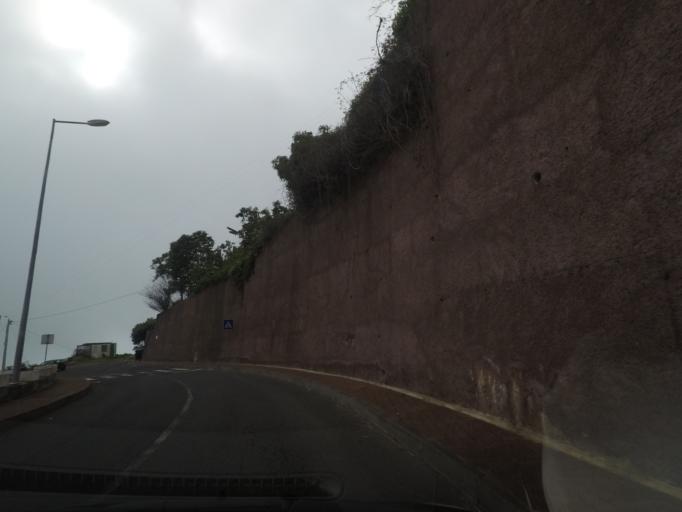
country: PT
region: Madeira
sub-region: Ribeira Brava
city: Campanario
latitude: 32.6598
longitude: -17.0148
